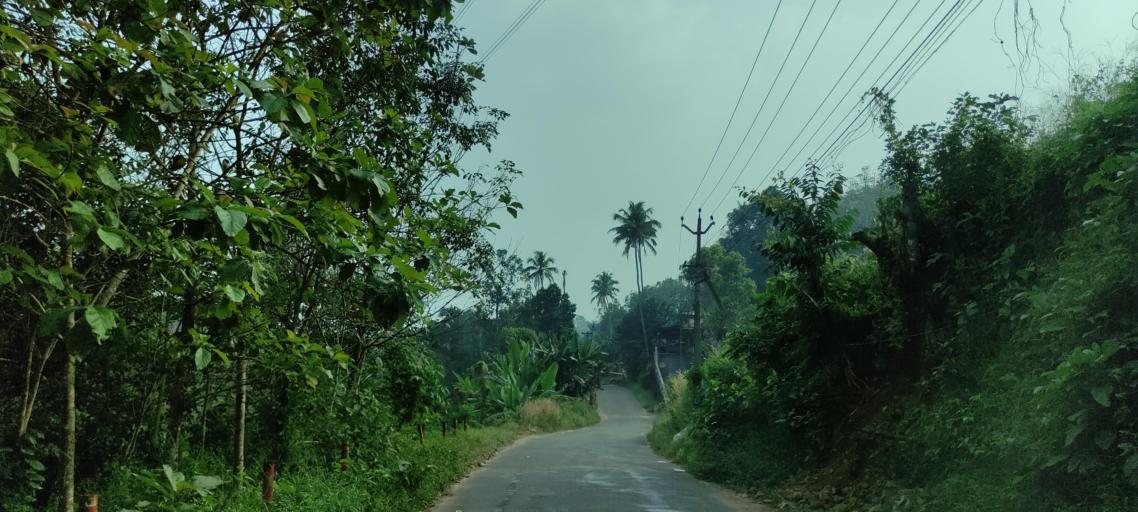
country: IN
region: Kerala
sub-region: Ernakulam
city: Piravam
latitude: 9.8025
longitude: 76.5354
